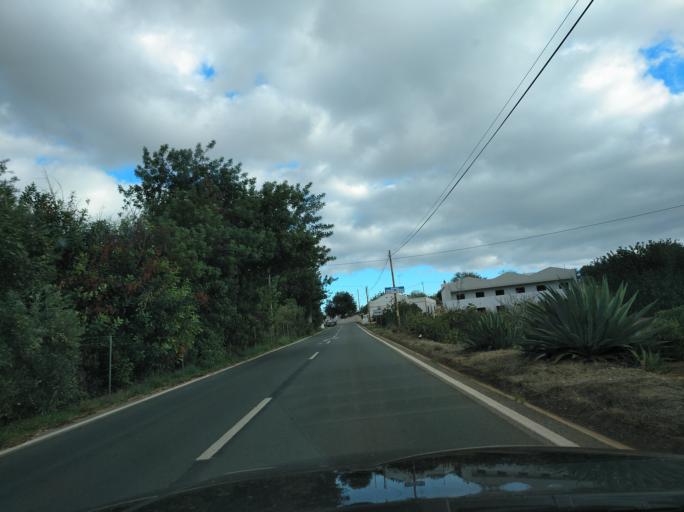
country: PT
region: Faro
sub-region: Tavira
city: Luz
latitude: 37.1413
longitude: -7.7145
